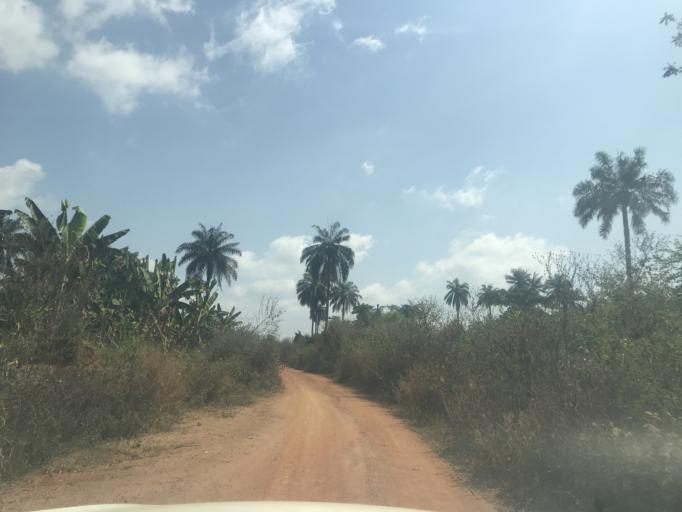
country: NG
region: Osun
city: Oke Mesi
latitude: 7.8885
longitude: 4.8834
